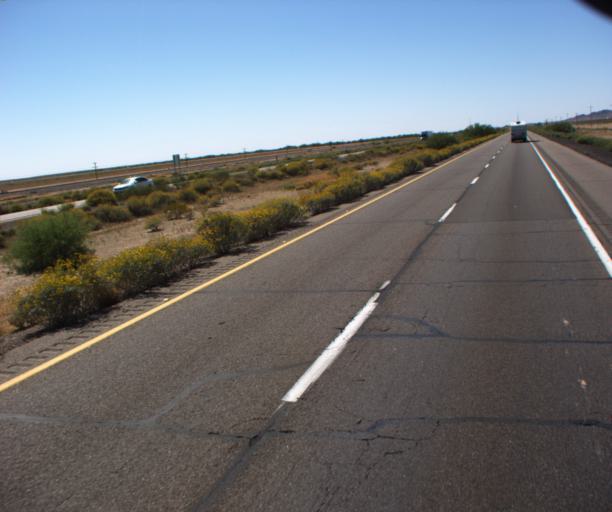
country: US
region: Arizona
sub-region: Maricopa County
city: Gila Bend
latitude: 32.9134
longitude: -112.9462
